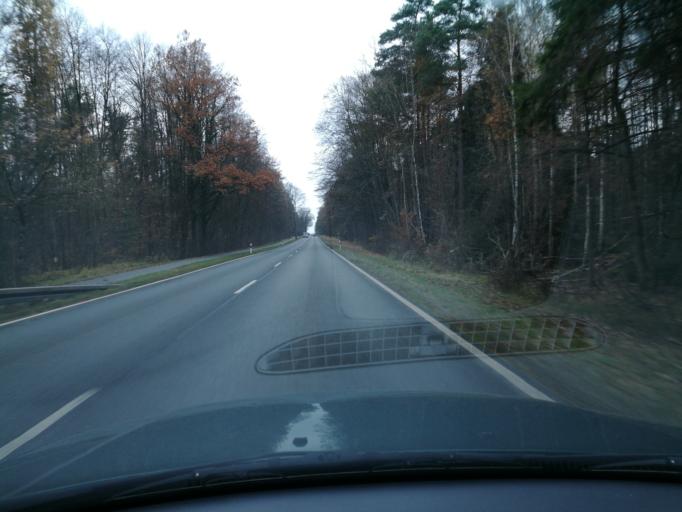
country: DE
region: Bavaria
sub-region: Regierungsbezirk Mittelfranken
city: Feucht
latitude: 49.3860
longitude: 11.1987
